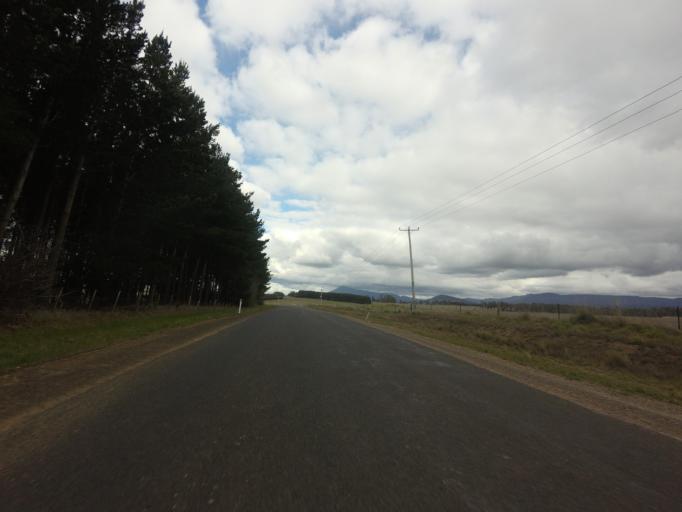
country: AU
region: Tasmania
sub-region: Northern Midlands
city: Longford
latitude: -41.7724
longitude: 147.0895
